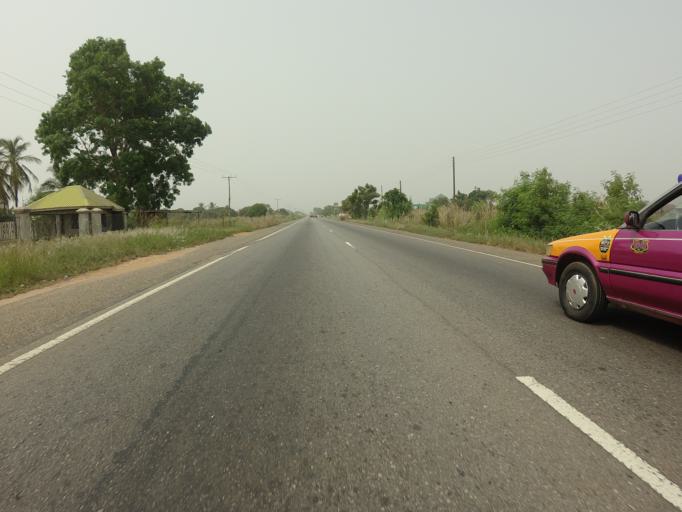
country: GH
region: Volta
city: Anloga
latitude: 5.8939
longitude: 0.5007
